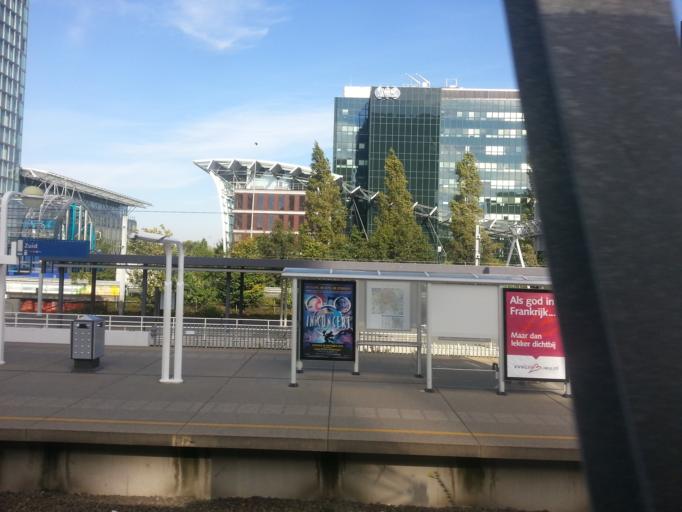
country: NL
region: North Holland
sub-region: Gemeente Amsterdam
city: Amsterdam
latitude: 52.3390
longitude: 4.8740
